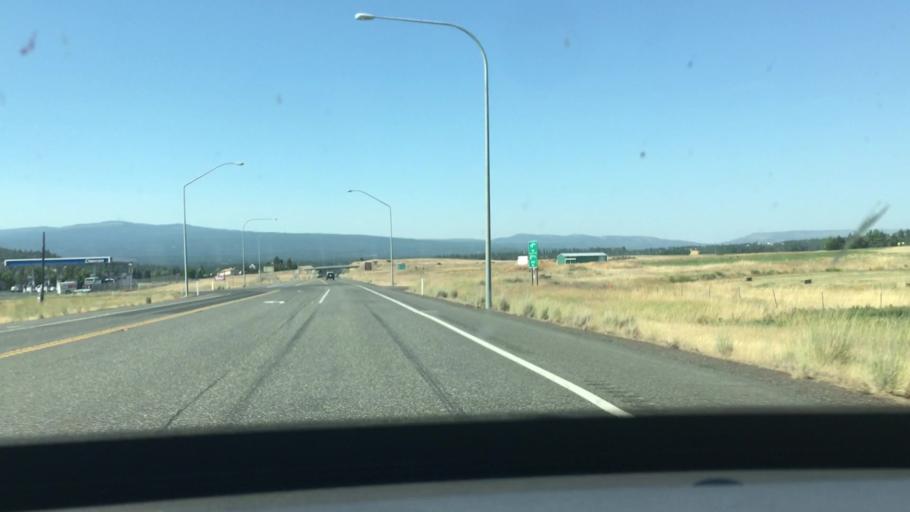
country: US
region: Washington
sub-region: Klickitat County
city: Goldendale
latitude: 45.8115
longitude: -120.8073
